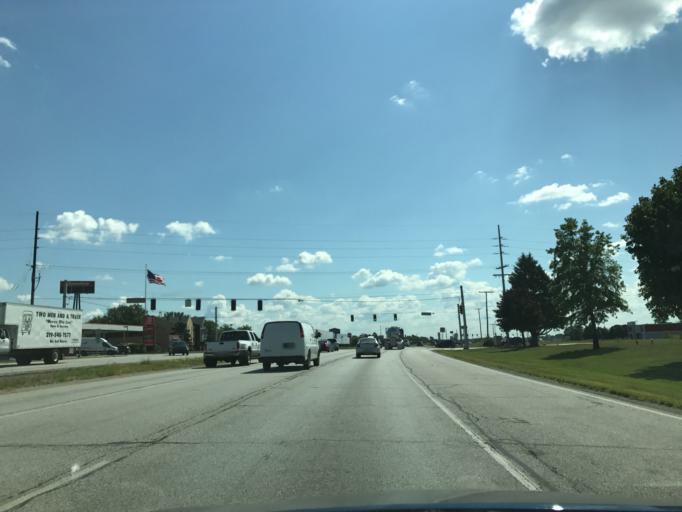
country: US
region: Indiana
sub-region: Porter County
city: Valparaiso
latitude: 41.4603
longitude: -87.0381
